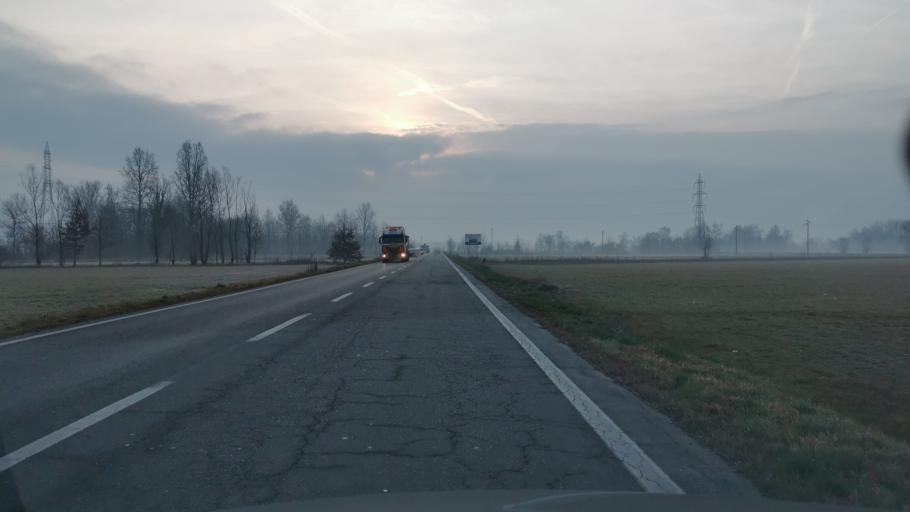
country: IT
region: Piedmont
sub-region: Provincia di Torino
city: Ciconio
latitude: 45.3405
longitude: 7.7751
